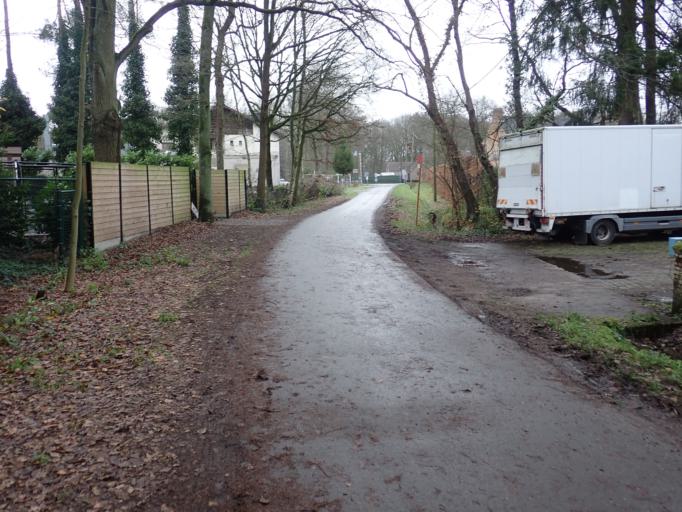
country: BE
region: Flanders
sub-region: Provincie Antwerpen
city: Schilde
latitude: 51.2457
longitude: 4.6256
